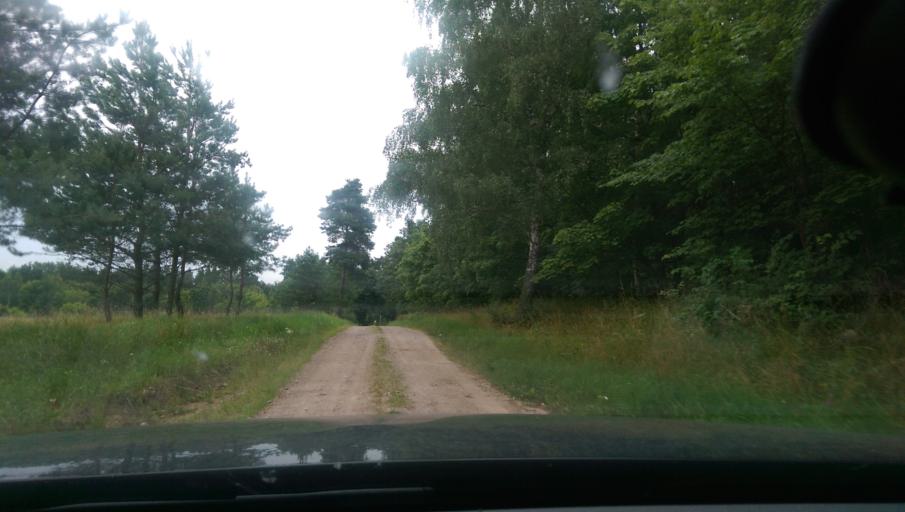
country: PL
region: Warmian-Masurian Voivodeship
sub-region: Powiat piski
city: Orzysz
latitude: 53.8230
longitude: 21.8108
